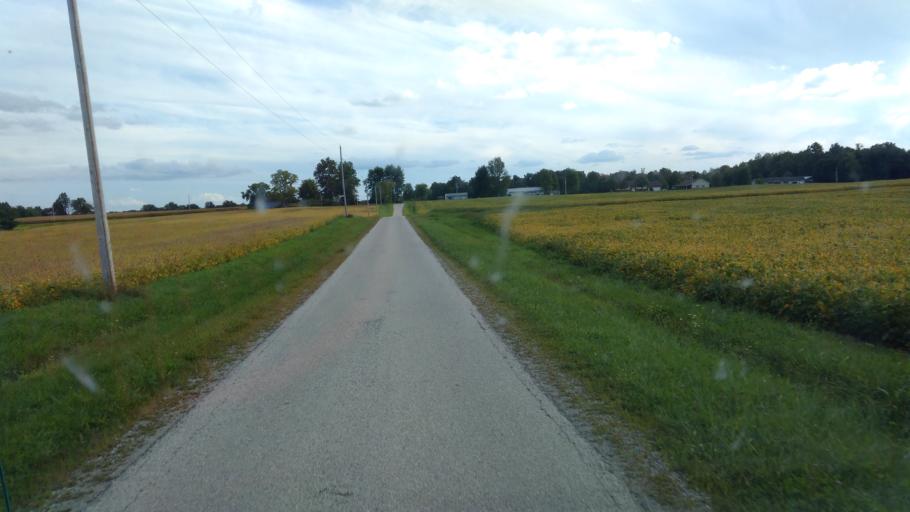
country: US
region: Ohio
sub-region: Crawford County
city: Bucyrus
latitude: 40.9100
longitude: -82.9783
